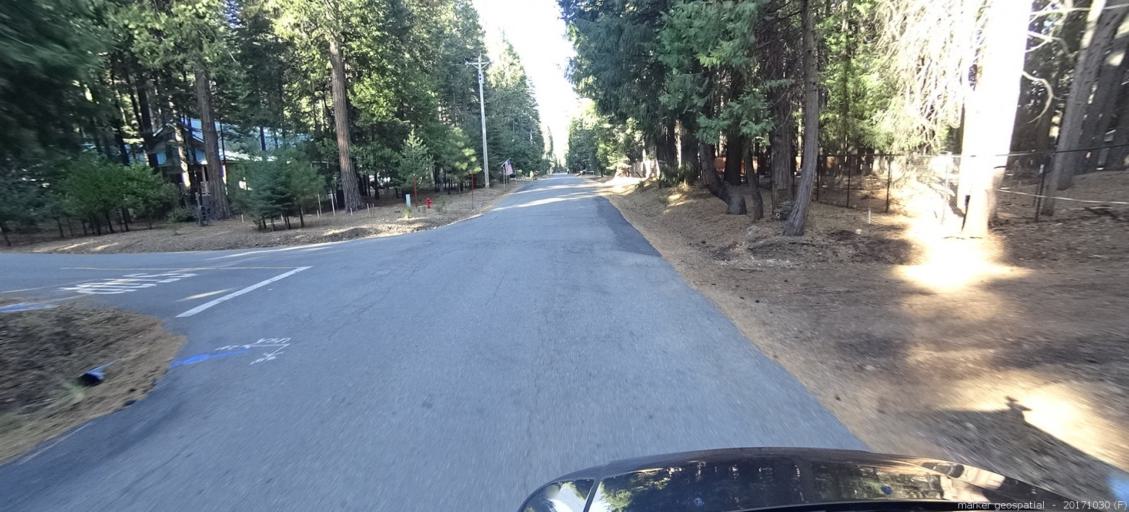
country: US
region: California
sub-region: Shasta County
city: Shingletown
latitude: 40.5522
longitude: -121.7281
